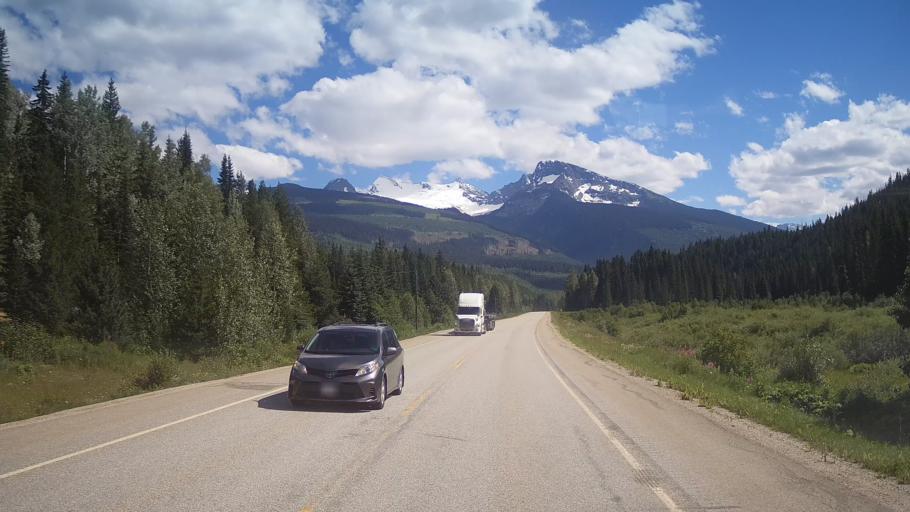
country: CA
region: Alberta
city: Jasper Park Lodge
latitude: 52.5940
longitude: -119.1014
